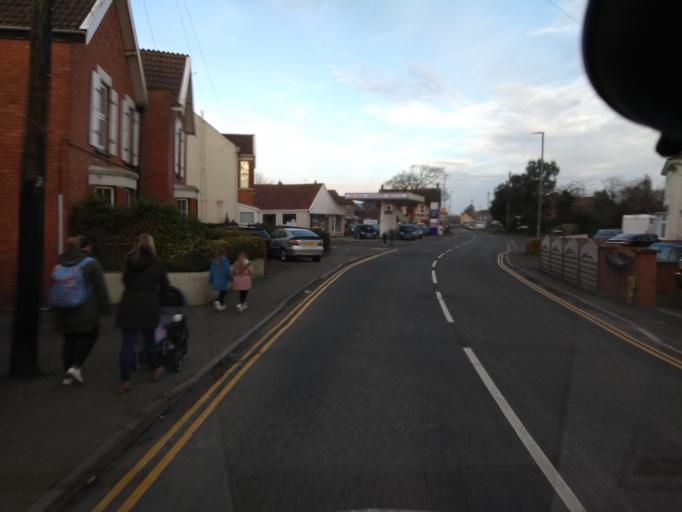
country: GB
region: England
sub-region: Somerset
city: Burnham-on-Sea
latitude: 51.2575
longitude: -3.0037
